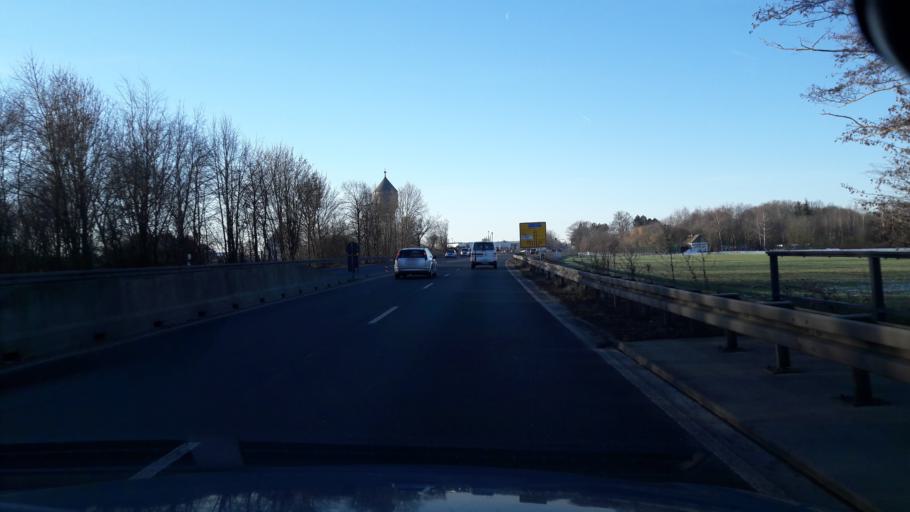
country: DE
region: North Rhine-Westphalia
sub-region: Regierungsbezirk Arnsberg
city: Lippstadt
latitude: 51.6652
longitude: 8.3656
